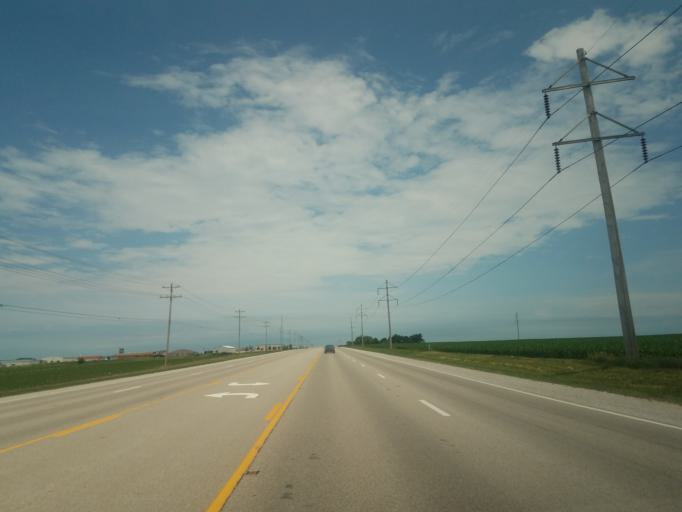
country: US
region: Illinois
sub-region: McLean County
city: Downs
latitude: 40.4628
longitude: -88.9019
